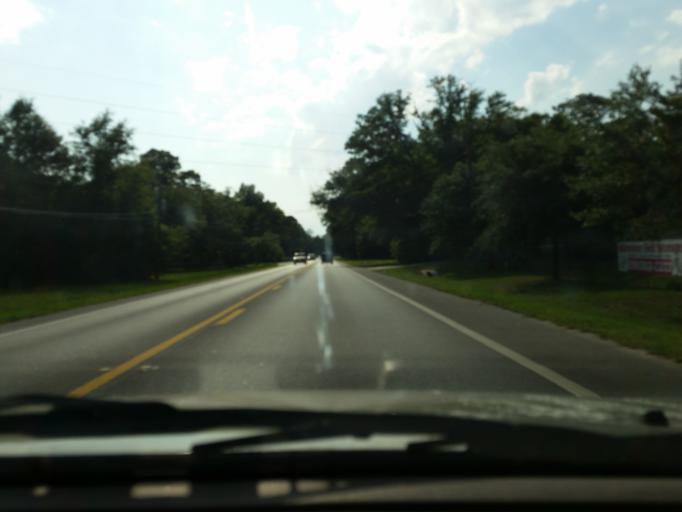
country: US
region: Florida
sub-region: Escambia County
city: Ensley
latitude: 30.5370
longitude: -87.3143
